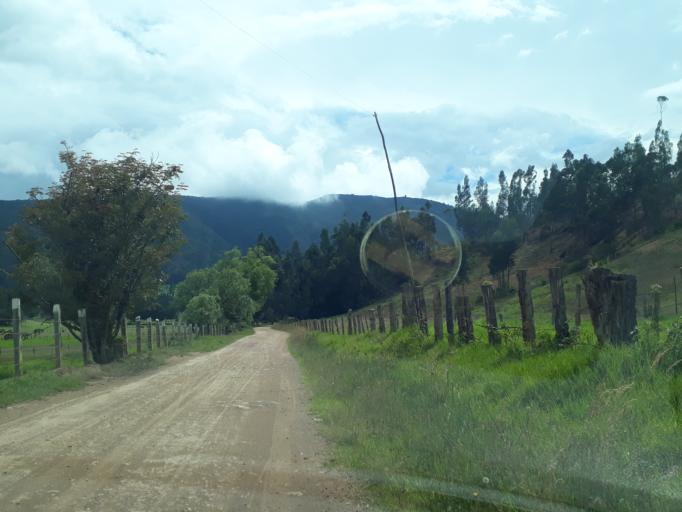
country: CO
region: Boyaca
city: Floresta
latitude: 5.8560
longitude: -72.9472
